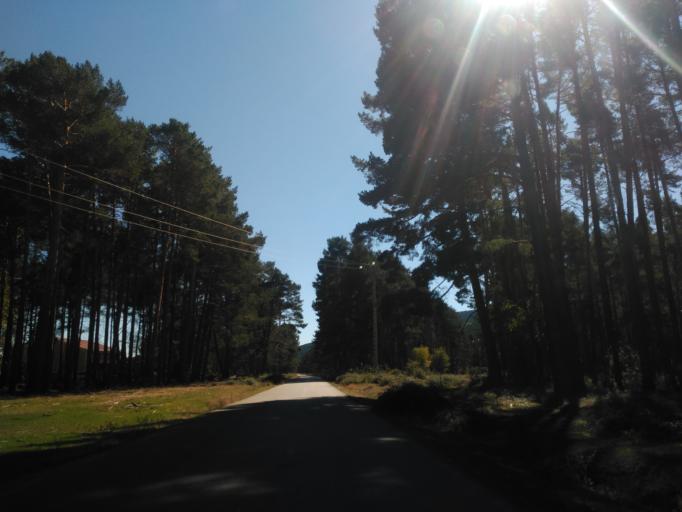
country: ES
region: Castille and Leon
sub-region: Provincia de Soria
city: Vinuesa
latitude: 41.9406
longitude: -2.7794
